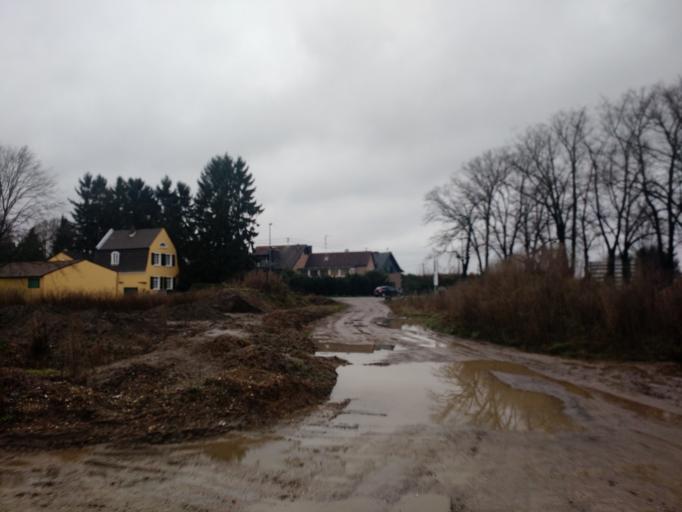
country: DE
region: North Rhine-Westphalia
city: Bruhl
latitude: 50.8529
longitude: 6.9216
